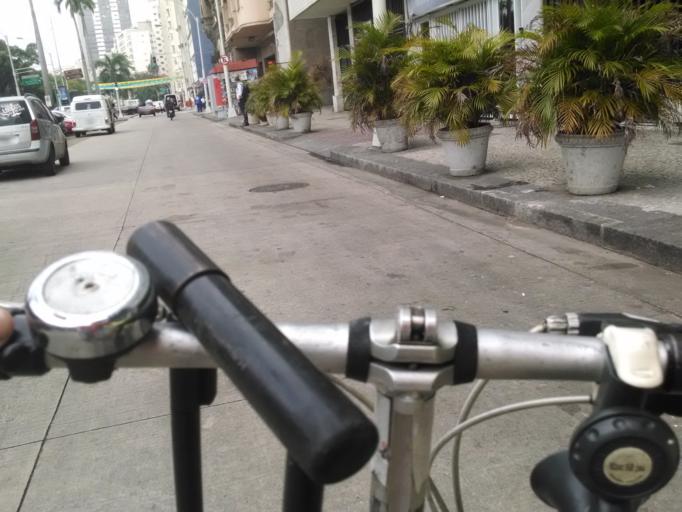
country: BR
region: Rio de Janeiro
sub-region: Rio De Janeiro
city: Rio de Janeiro
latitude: -22.9270
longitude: -43.1736
